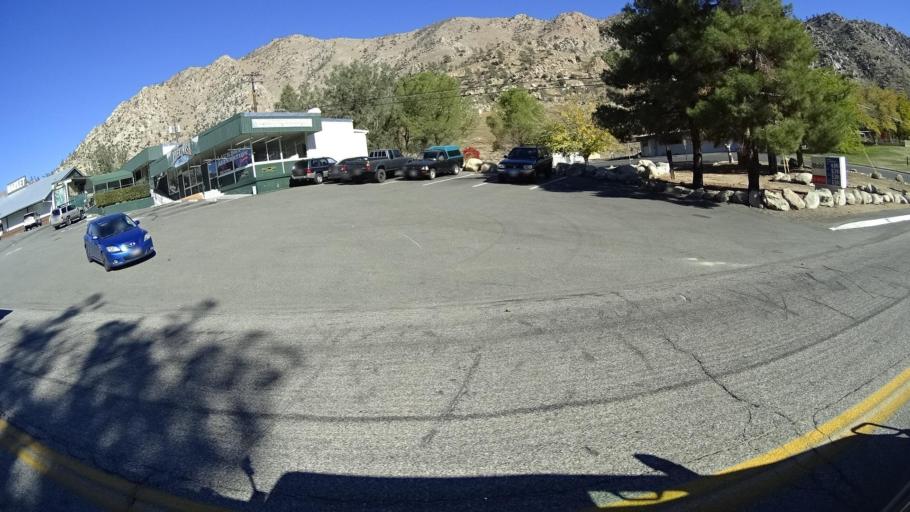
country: US
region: California
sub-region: Kern County
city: Kernville
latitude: 35.7567
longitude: -118.4205
